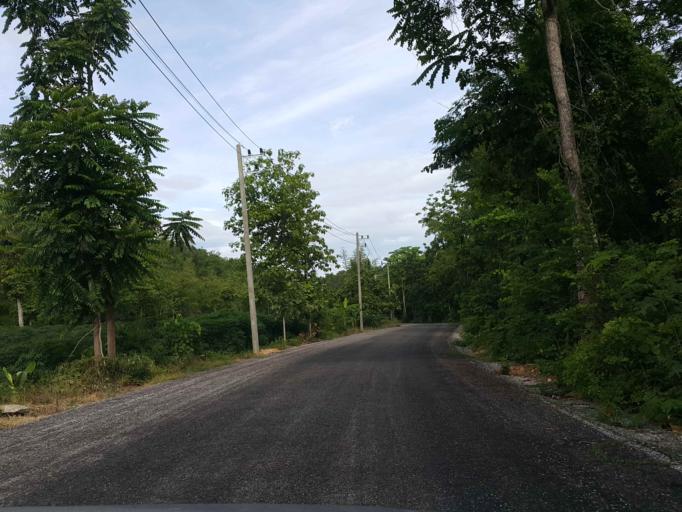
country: TH
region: Sukhothai
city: Thung Saliam
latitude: 17.2600
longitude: 99.5211
